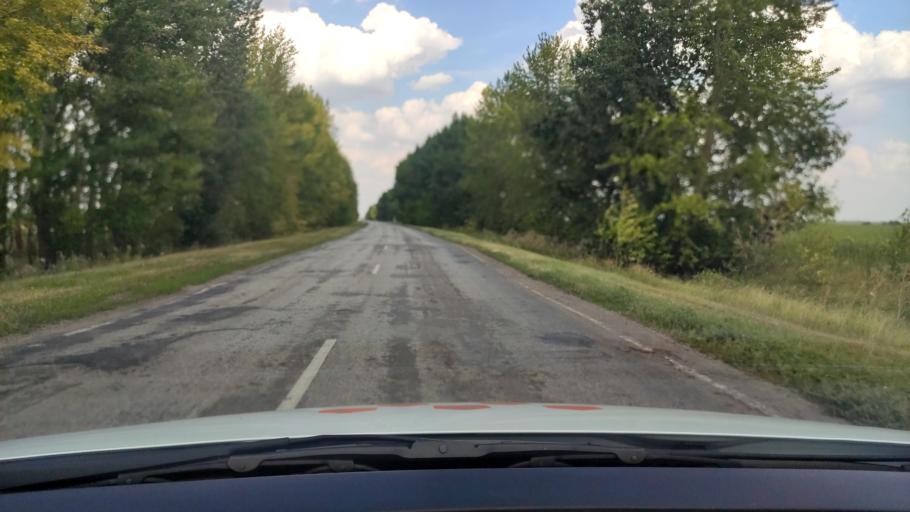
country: RU
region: Voronezj
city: Pereleshinskiy
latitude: 51.7273
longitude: 40.3732
